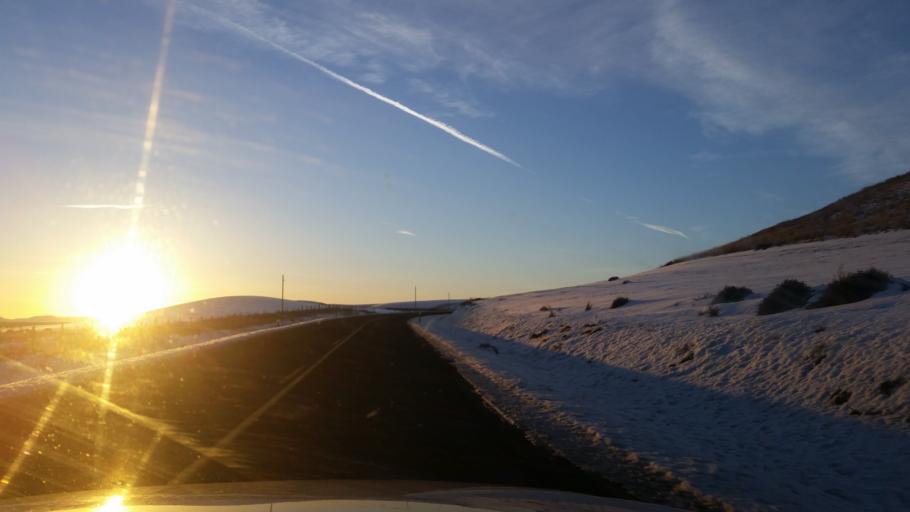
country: US
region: Washington
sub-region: Spokane County
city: Cheney
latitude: 47.1114
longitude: -117.8124
